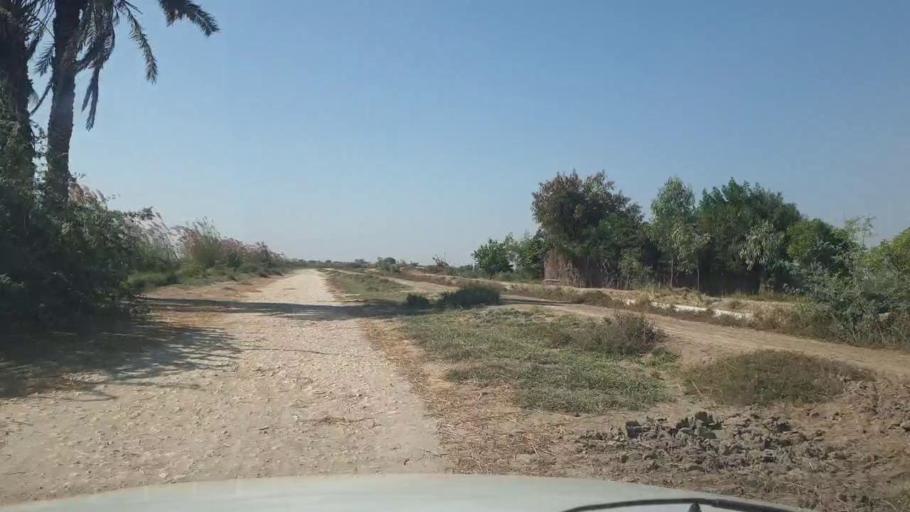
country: PK
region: Sindh
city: Chuhar Jamali
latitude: 24.4240
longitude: 67.7941
